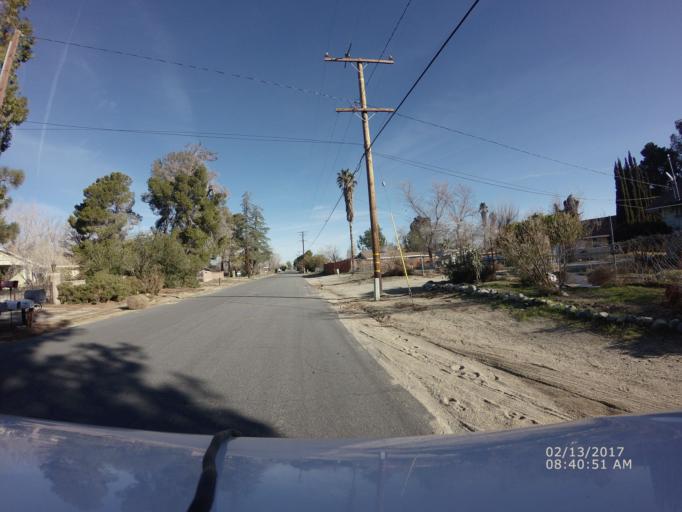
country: US
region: California
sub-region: Los Angeles County
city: Littlerock
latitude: 34.5239
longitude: -117.9881
